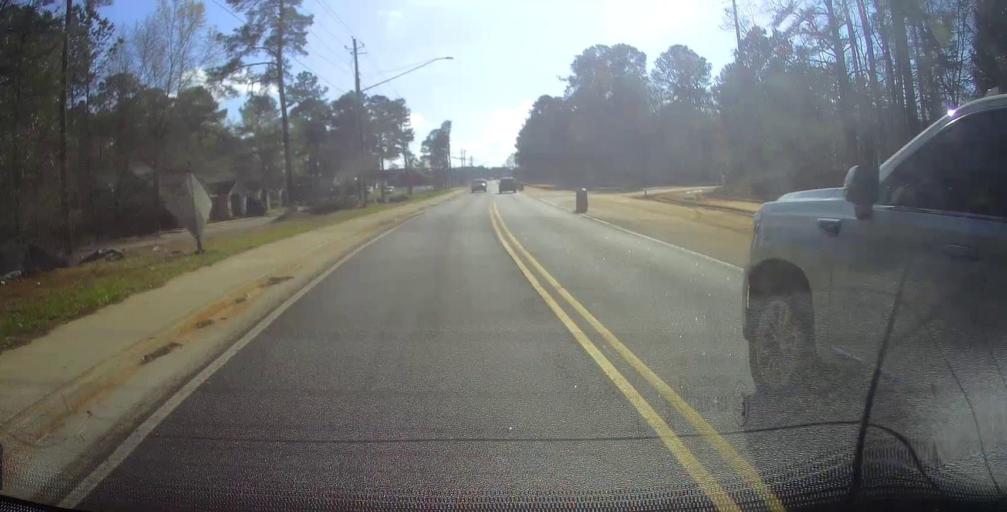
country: US
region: Georgia
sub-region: Laurens County
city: Dublin
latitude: 32.5368
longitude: -82.9484
